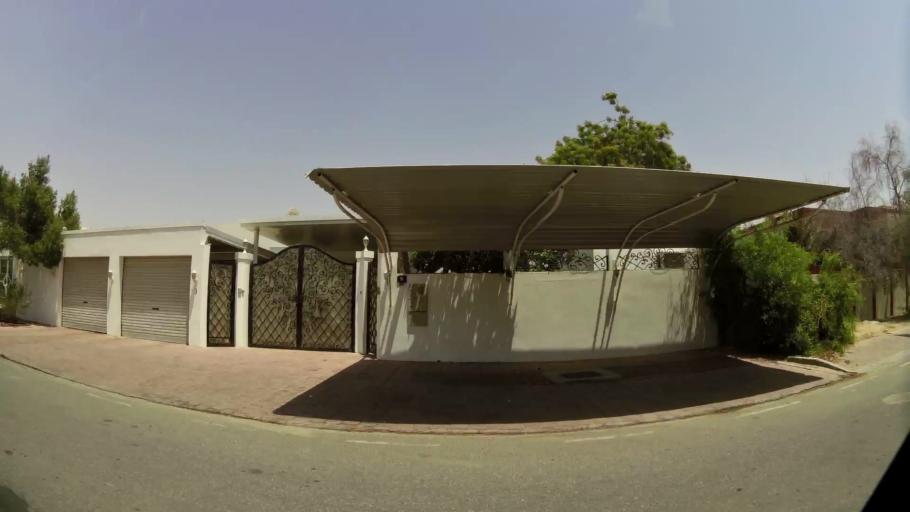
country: AE
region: Dubai
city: Dubai
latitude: 25.1578
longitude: 55.2080
